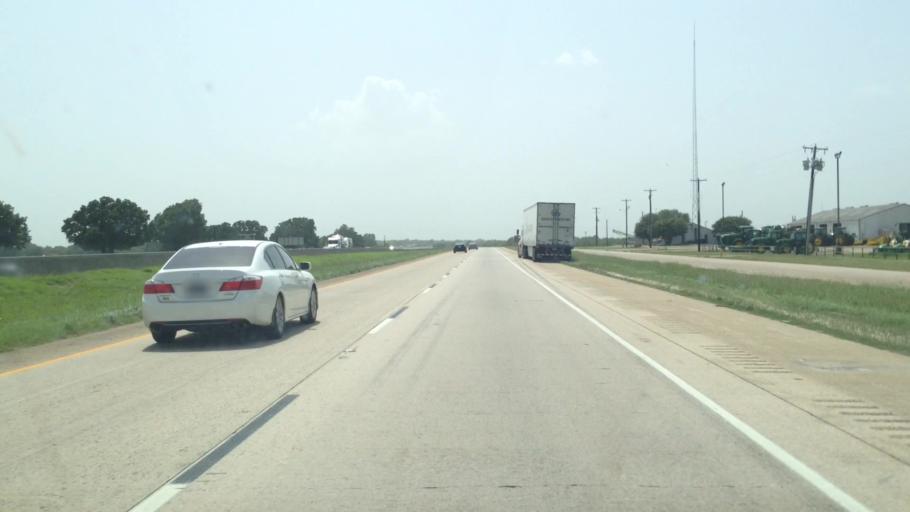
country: US
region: Texas
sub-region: Hopkins County
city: Sulphur Springs
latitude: 33.1209
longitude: -95.7009
